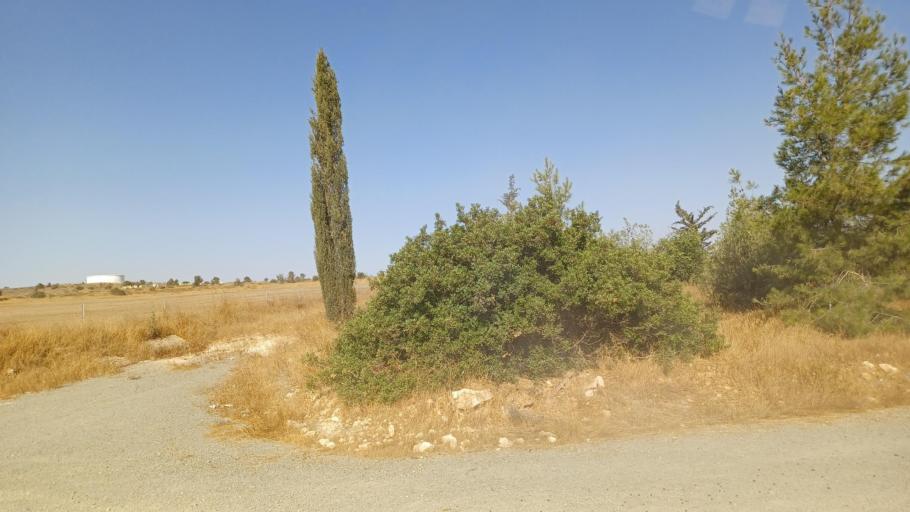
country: CY
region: Larnaka
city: Athienou
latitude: 35.0230
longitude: 33.5475
